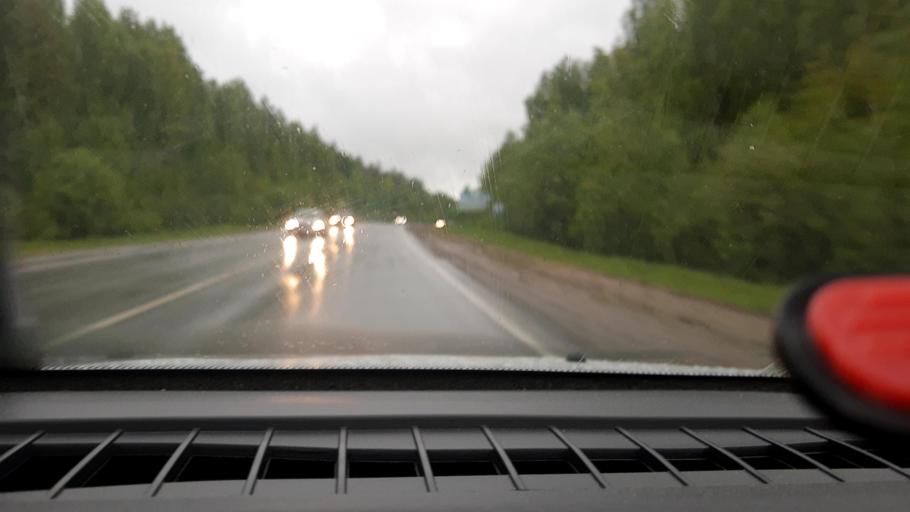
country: RU
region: Nizjnij Novgorod
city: Semenov
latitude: 56.8071
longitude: 44.4643
